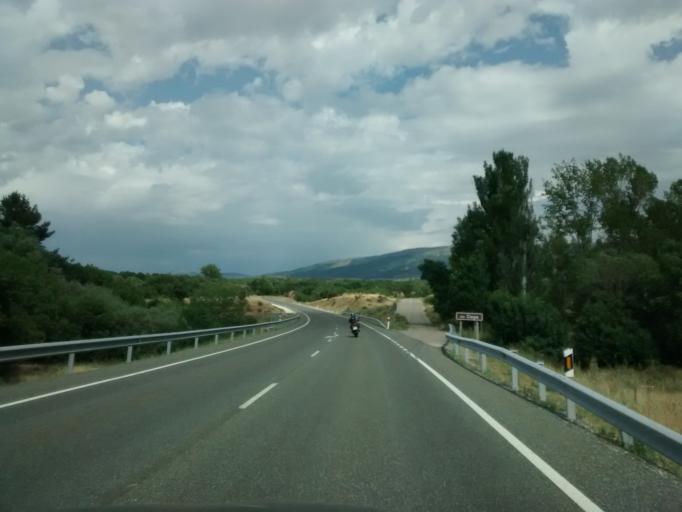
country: ES
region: Castille and Leon
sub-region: Provincia de Segovia
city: Navafria
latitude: 41.0641
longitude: -3.8273
